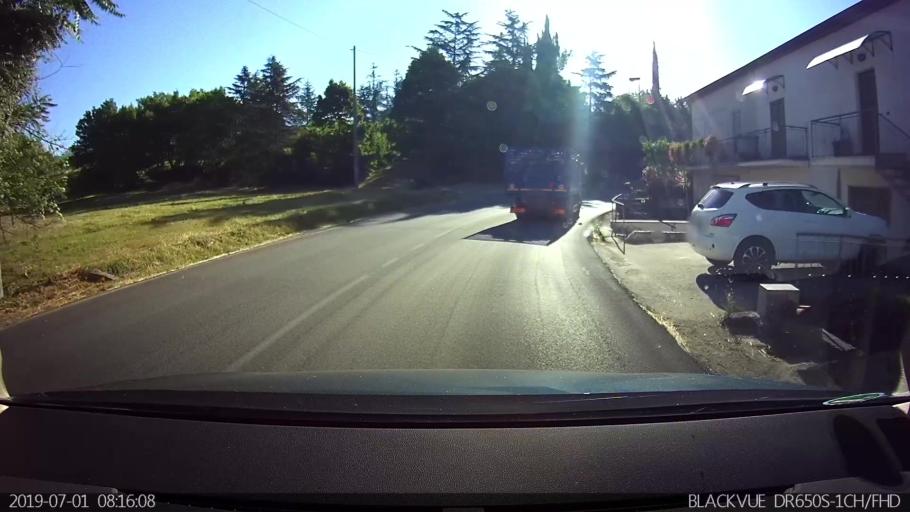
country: IT
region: Latium
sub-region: Provincia di Frosinone
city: Veroli
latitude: 41.7008
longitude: 13.4323
